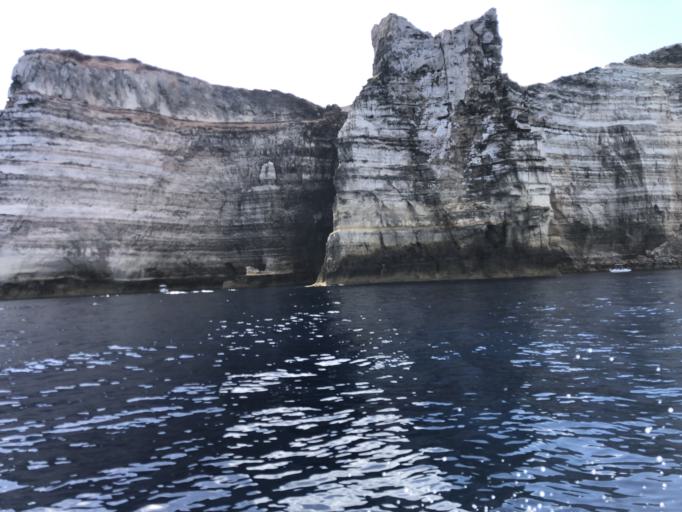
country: IT
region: Sicily
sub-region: Agrigento
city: Lampedusa
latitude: 35.5288
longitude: 12.5244
